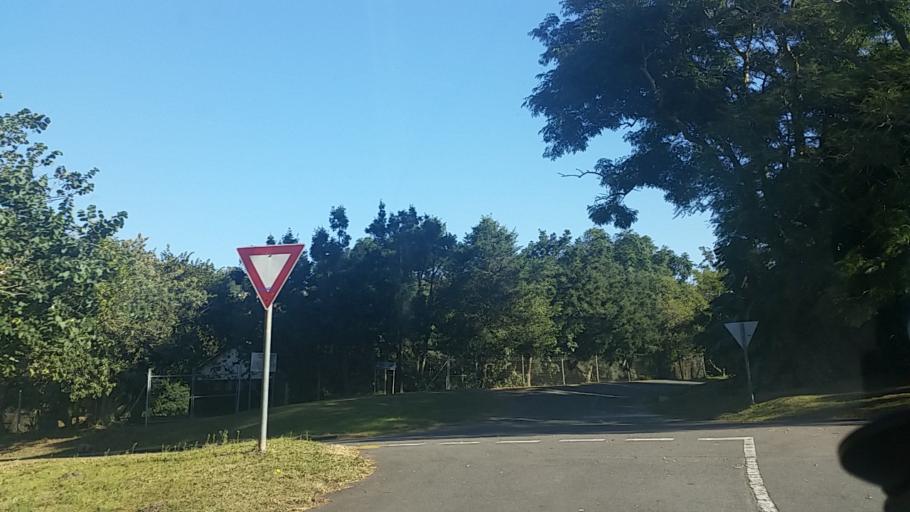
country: ZA
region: KwaZulu-Natal
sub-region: eThekwini Metropolitan Municipality
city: Berea
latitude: -29.8440
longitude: 30.9027
